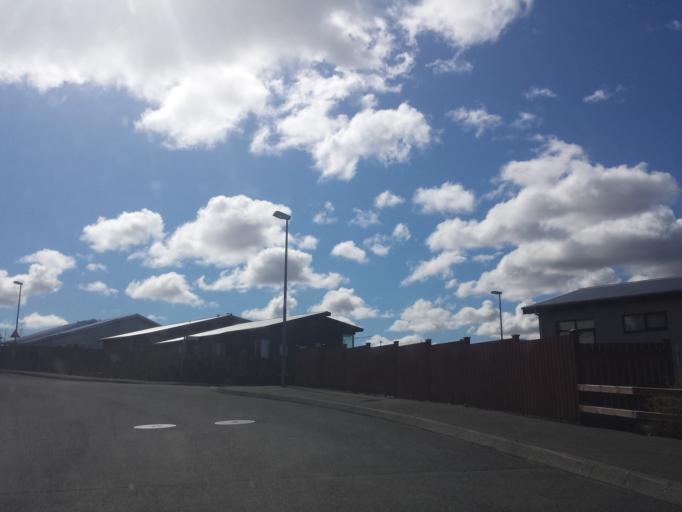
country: IS
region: Capital Region
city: Reykjavik
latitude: 64.0908
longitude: -21.8529
